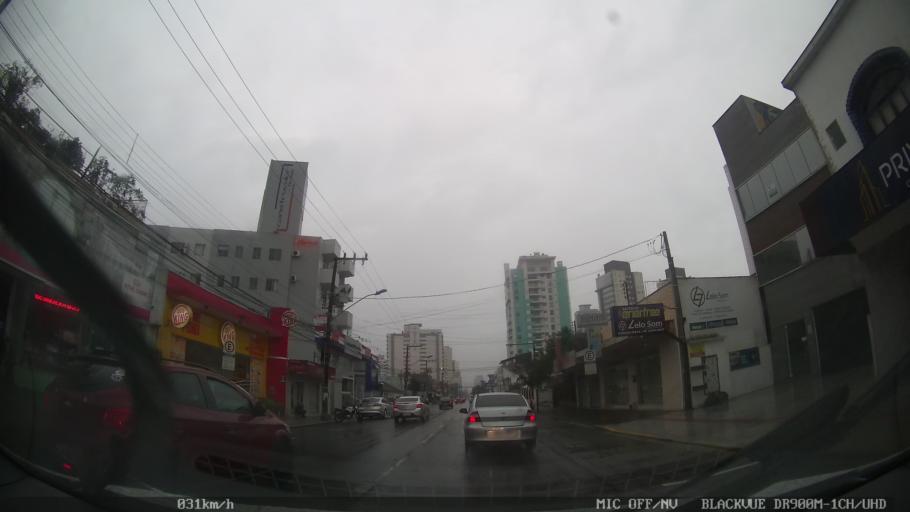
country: BR
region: Santa Catarina
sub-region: Itajai
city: Itajai
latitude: -26.9155
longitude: -48.6556
